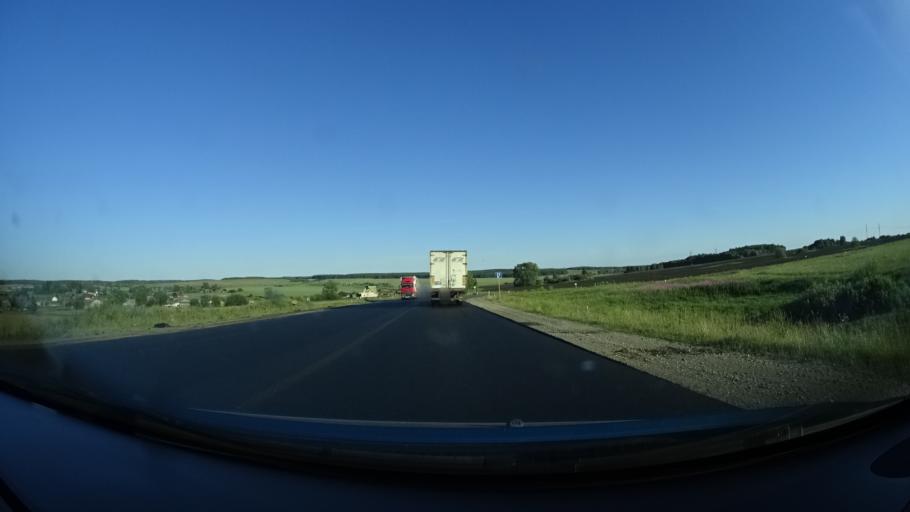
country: RU
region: Sverdlovsk
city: Achit
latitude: 56.8960
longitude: 57.6030
